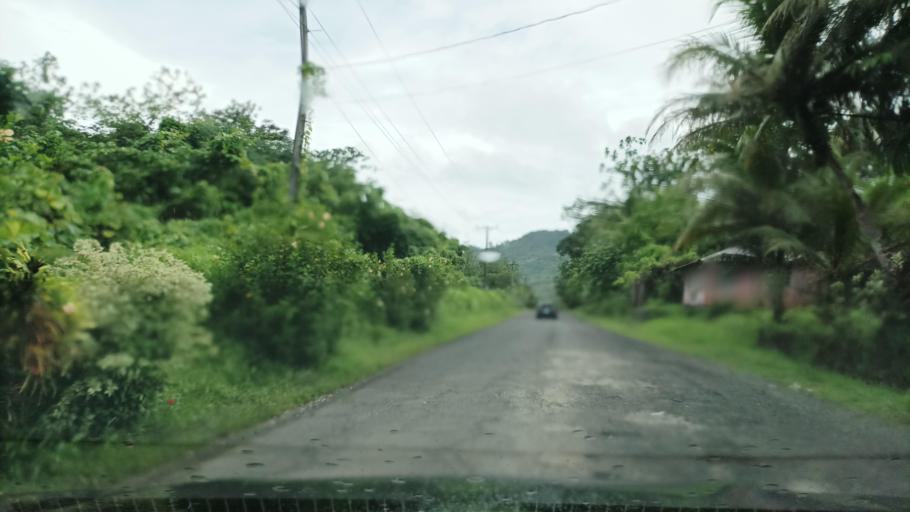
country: FM
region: Pohnpei
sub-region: Madolenihm Municipality
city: Madolenihm Municipality Government
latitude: 6.9228
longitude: 158.2869
